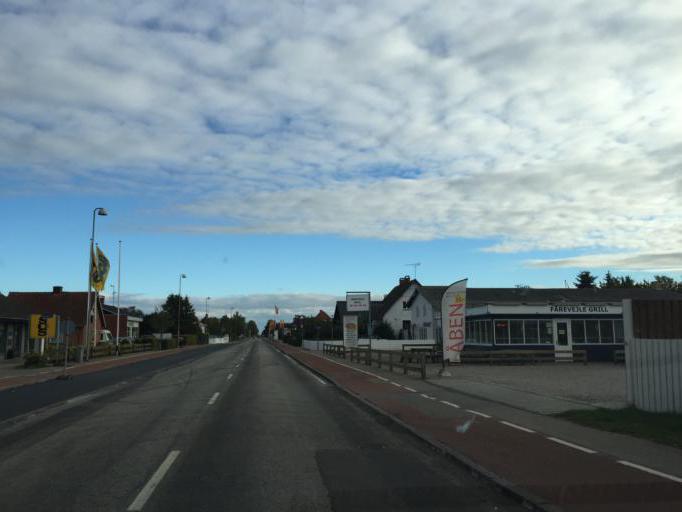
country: DK
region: Zealand
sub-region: Odsherred Kommune
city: Horve
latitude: 55.7880
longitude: 11.4644
